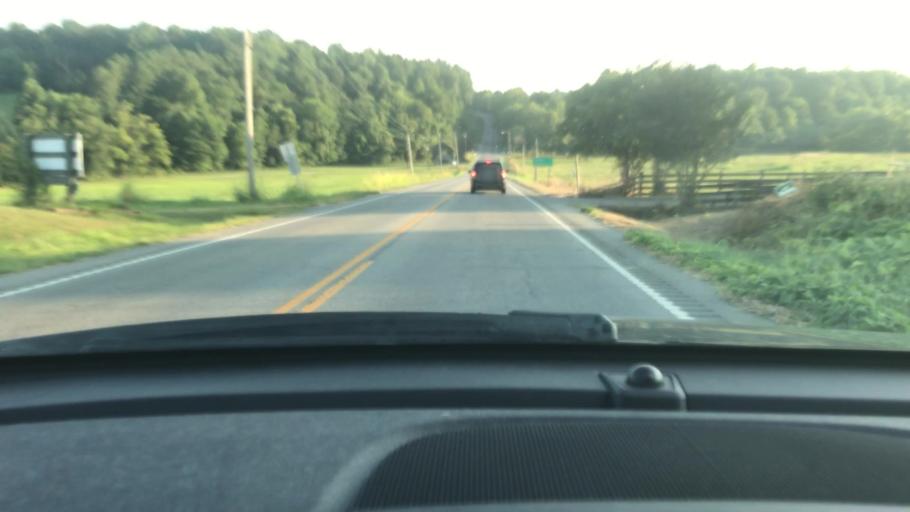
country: US
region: Tennessee
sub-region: Dickson County
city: Charlotte
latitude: 36.1649
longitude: -87.3524
